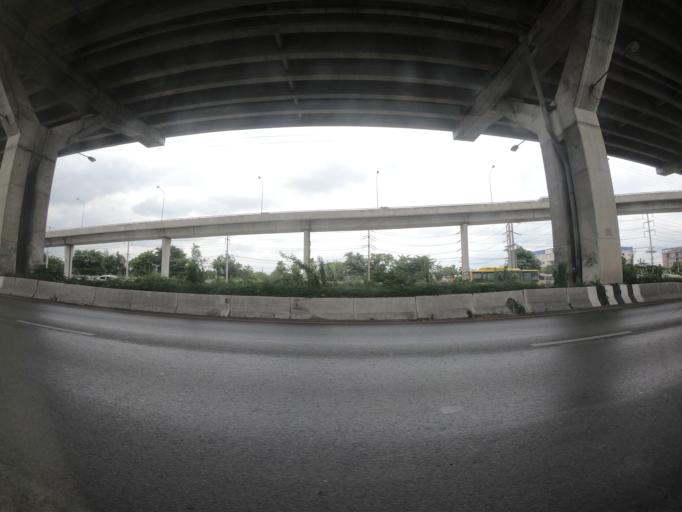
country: TH
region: Bangkok
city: Sai Mai
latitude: 13.9760
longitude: 100.6210
